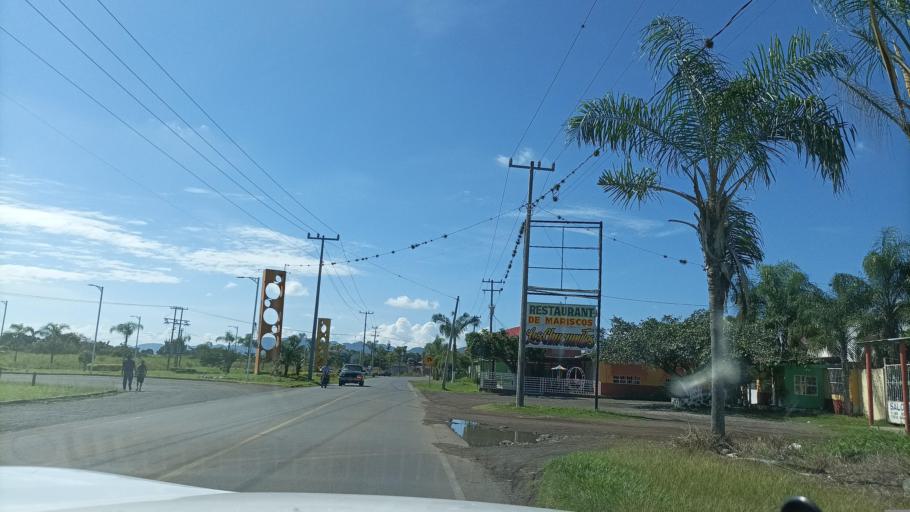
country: MX
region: Veracruz
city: Paso del Macho
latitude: 18.9653
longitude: -96.7340
